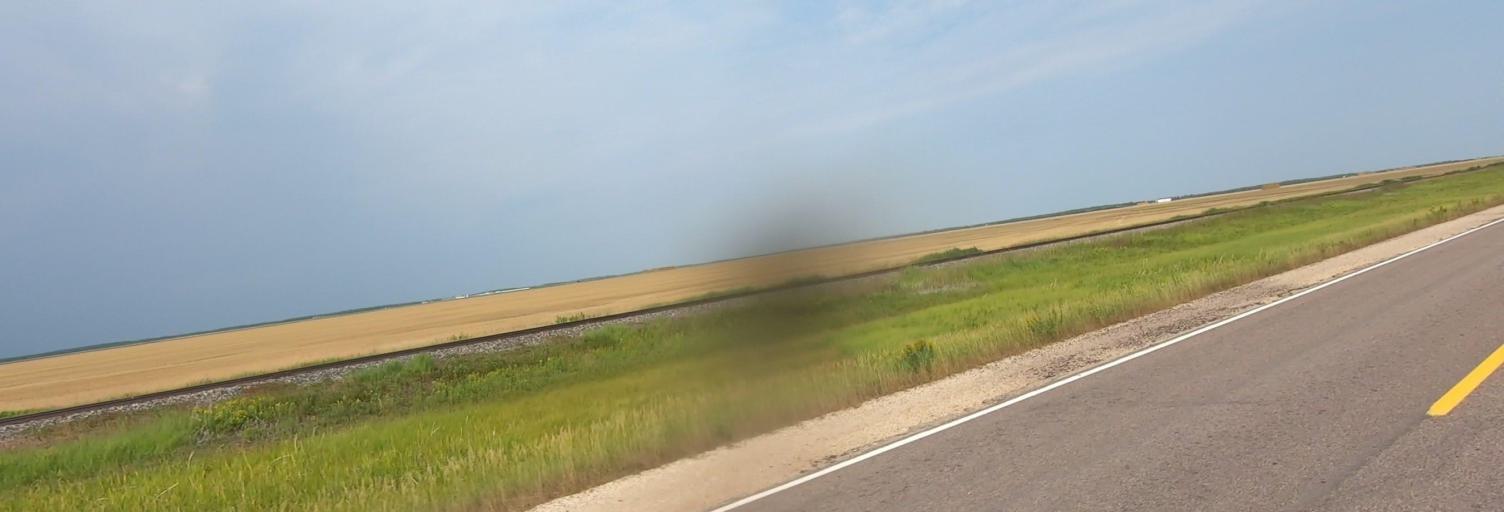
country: CA
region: Manitoba
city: Headingley
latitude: 49.6265
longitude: -97.3122
